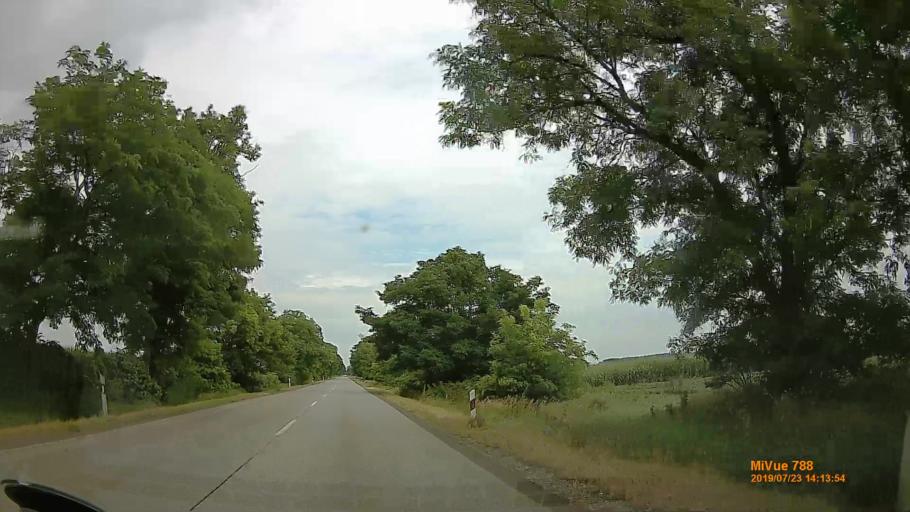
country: HU
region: Szabolcs-Szatmar-Bereg
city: Nagycserkesz
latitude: 47.9578
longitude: 21.4822
